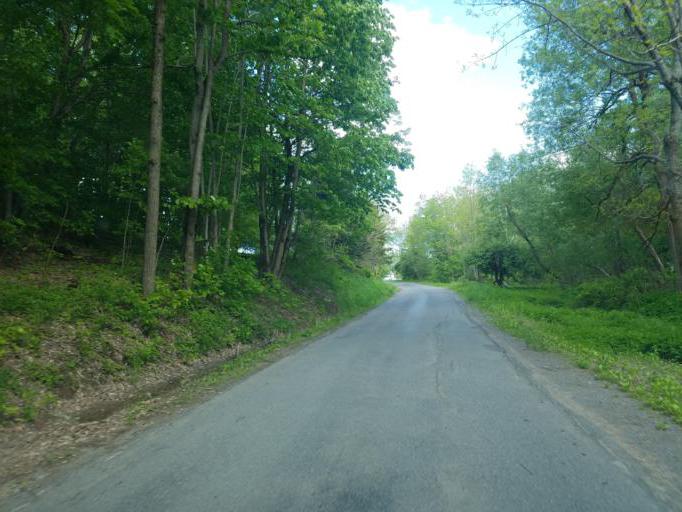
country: US
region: New York
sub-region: Herkimer County
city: Ilion
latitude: 42.9553
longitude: -75.0281
